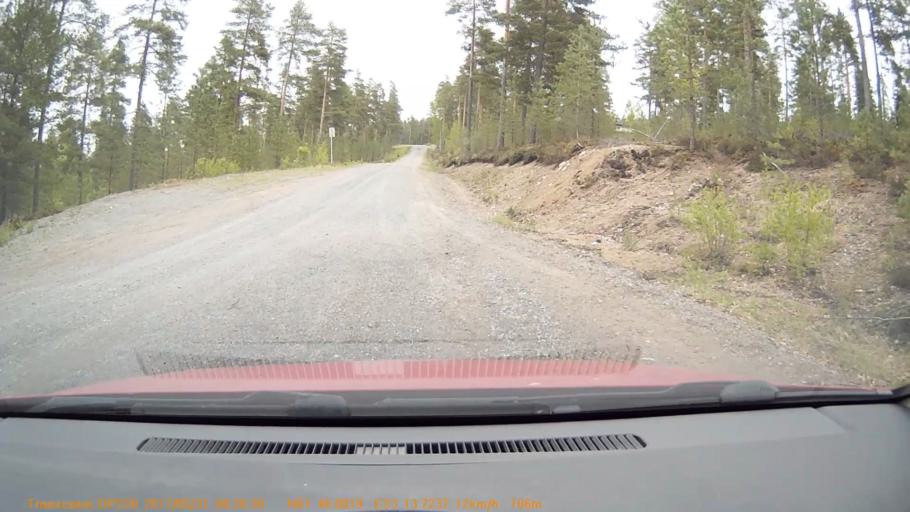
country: FI
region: Pirkanmaa
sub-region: Tampere
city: Haemeenkyroe
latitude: 61.6680
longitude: 23.2288
